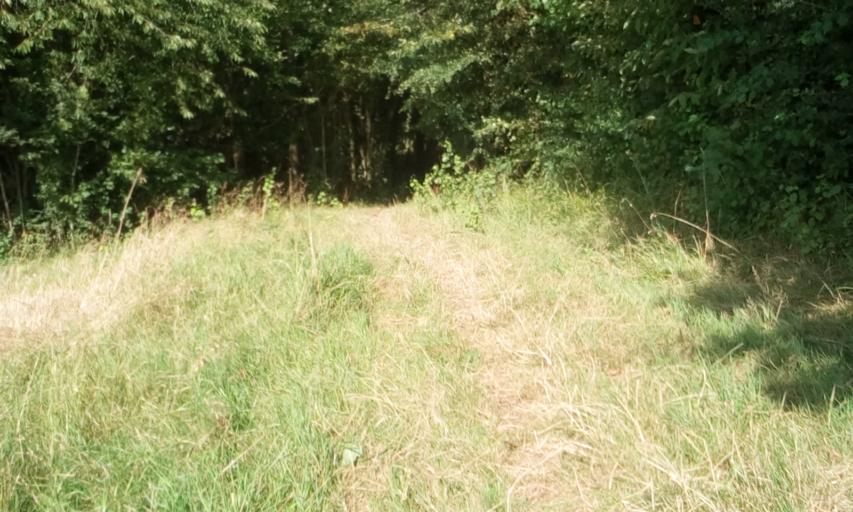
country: FR
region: Lower Normandy
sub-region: Departement du Calvados
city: Argences
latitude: 49.1417
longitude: -0.1111
